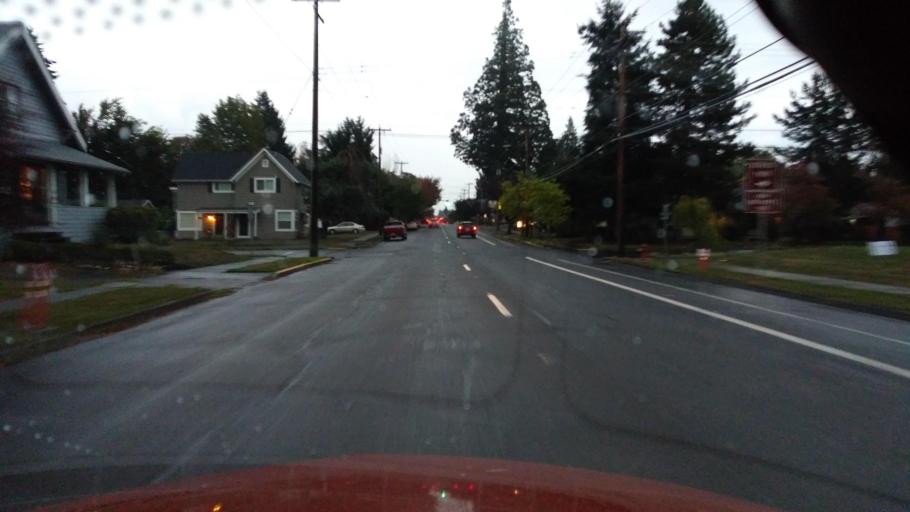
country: US
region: Oregon
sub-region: Washington County
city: Forest Grove
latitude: 45.5184
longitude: -123.1054
